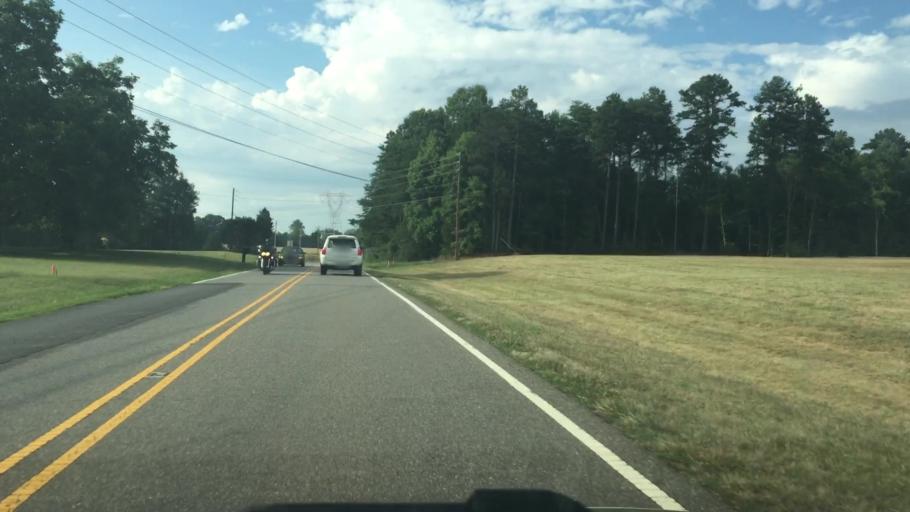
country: US
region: North Carolina
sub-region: Iredell County
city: Mooresville
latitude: 35.5320
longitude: -80.7691
